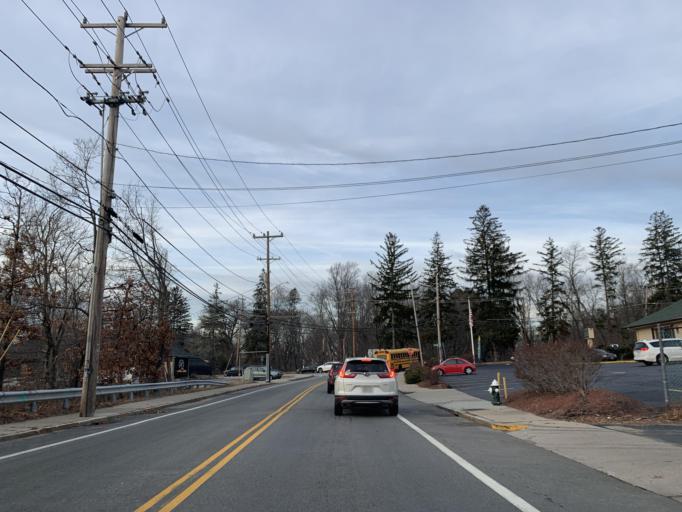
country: US
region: Rhode Island
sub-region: Providence County
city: Greenville
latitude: 41.8703
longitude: -71.5514
